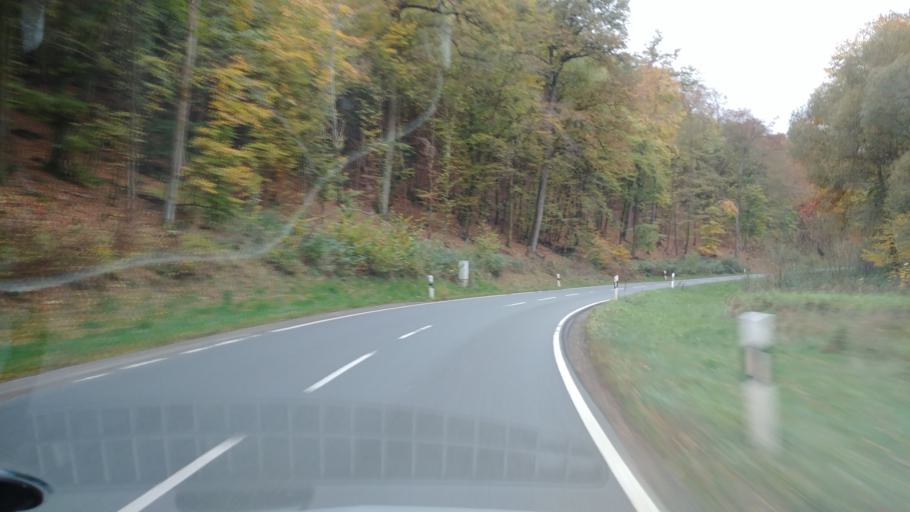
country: DE
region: Hesse
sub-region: Regierungsbezirk Darmstadt
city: Idstein
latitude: 50.2485
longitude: 8.2300
